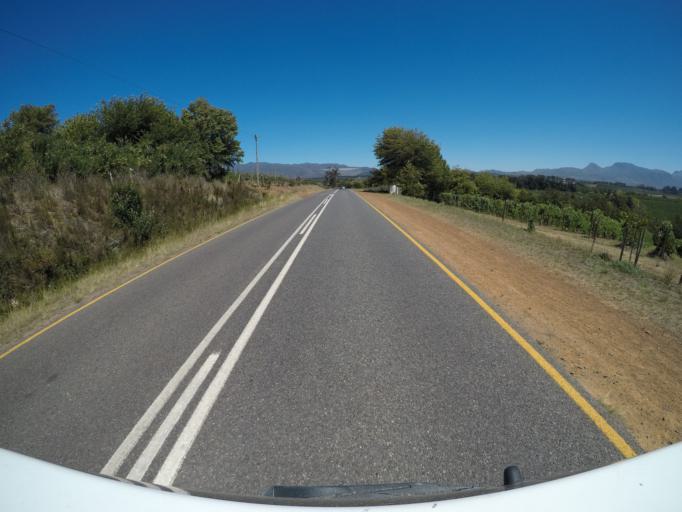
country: ZA
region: Western Cape
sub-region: Overberg District Municipality
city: Grabouw
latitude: -34.2086
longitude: 19.0408
